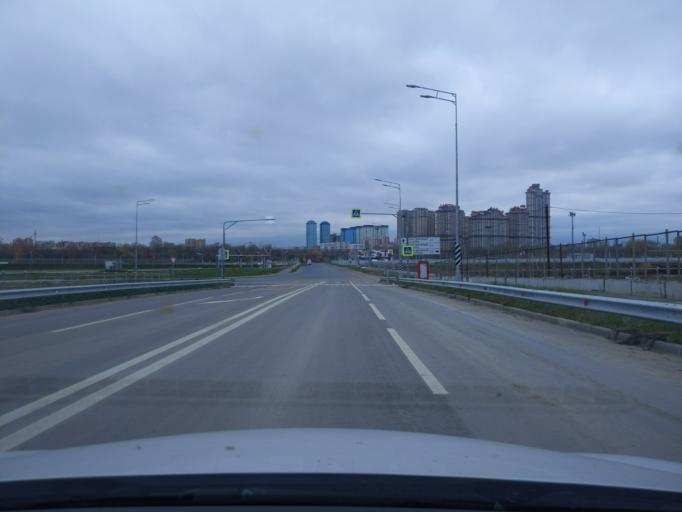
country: RU
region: Moscow
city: Strogino
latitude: 55.8149
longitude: 37.4325
